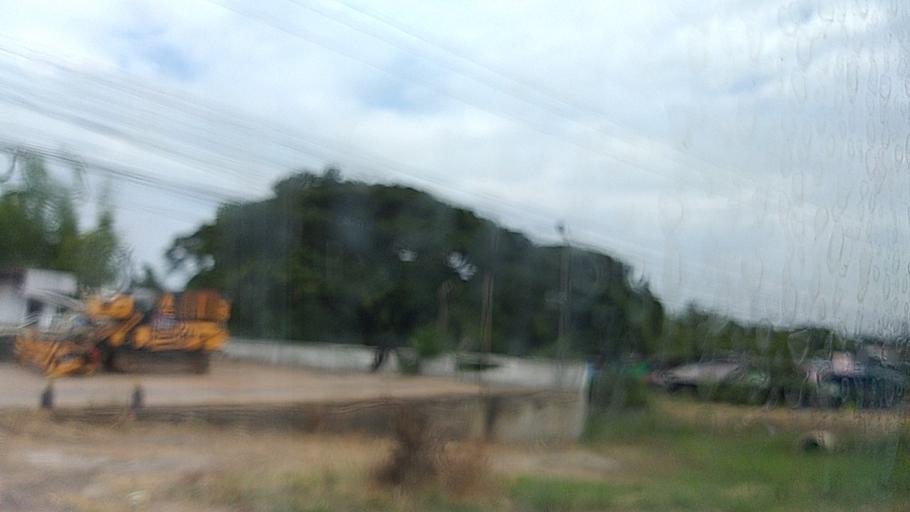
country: TH
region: Roi Et
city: Changhan
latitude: 16.1189
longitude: 103.4890
